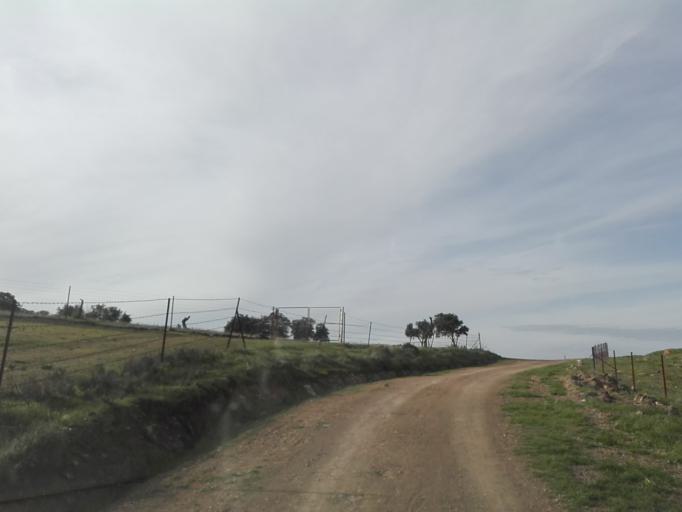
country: ES
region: Extremadura
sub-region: Provincia de Badajoz
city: Llerena
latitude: 38.2132
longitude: -6.0403
